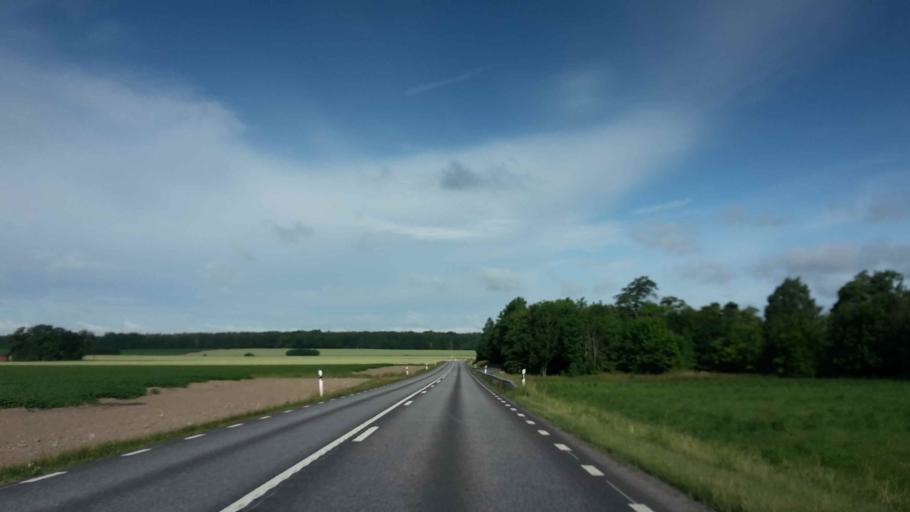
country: SE
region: OEstergoetland
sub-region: Motala Kommun
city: Borensberg
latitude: 58.5344
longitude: 15.3387
